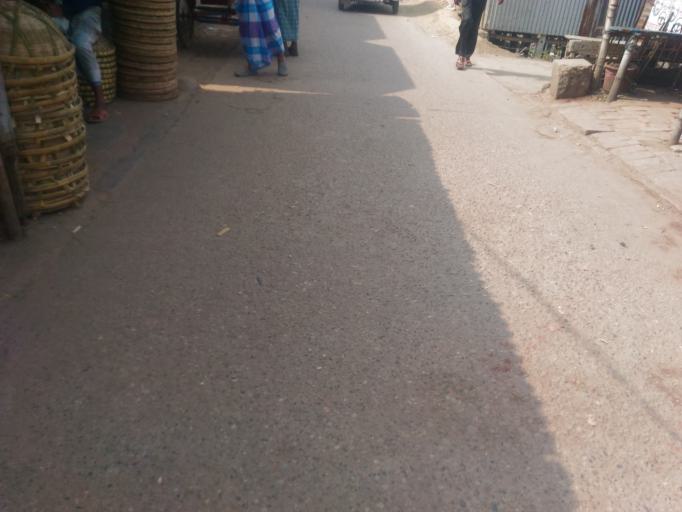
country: BD
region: Dhaka
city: Narayanganj
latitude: 23.6579
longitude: 90.4533
